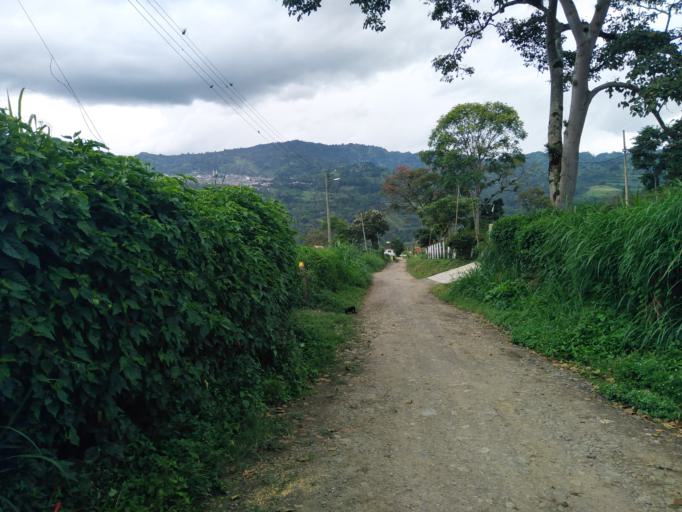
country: CO
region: Cundinamarca
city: Tenza
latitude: 5.0886
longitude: -73.3934
